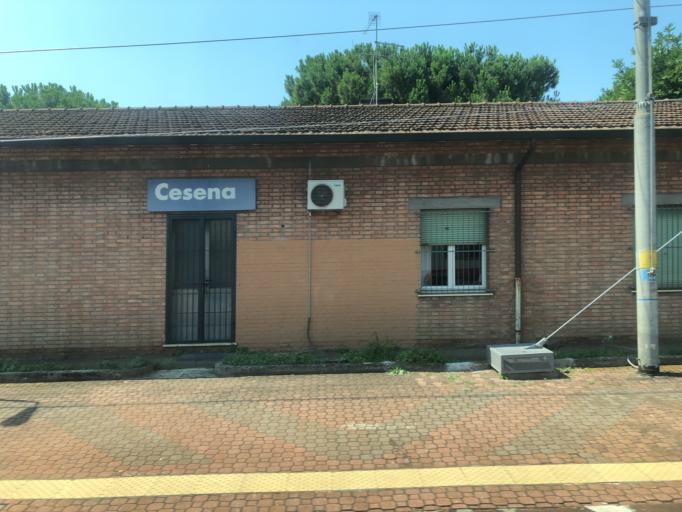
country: IT
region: Emilia-Romagna
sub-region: Forli-Cesena
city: Cesena
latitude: 44.1448
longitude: 12.2517
